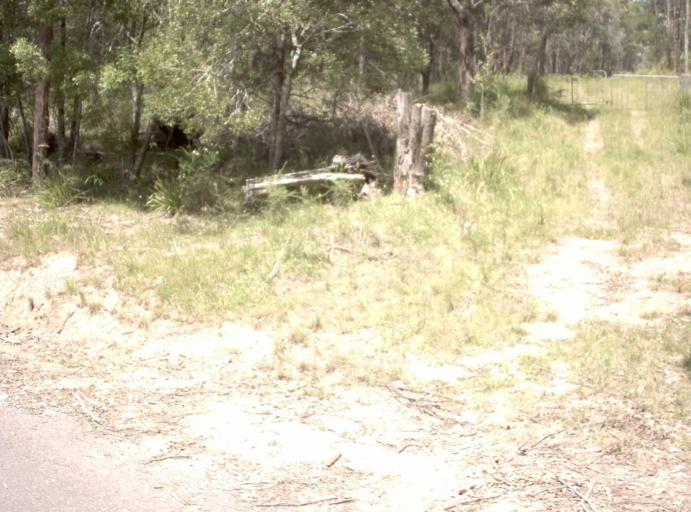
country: AU
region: New South Wales
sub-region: Bombala
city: Bombala
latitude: -37.4291
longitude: 149.0053
